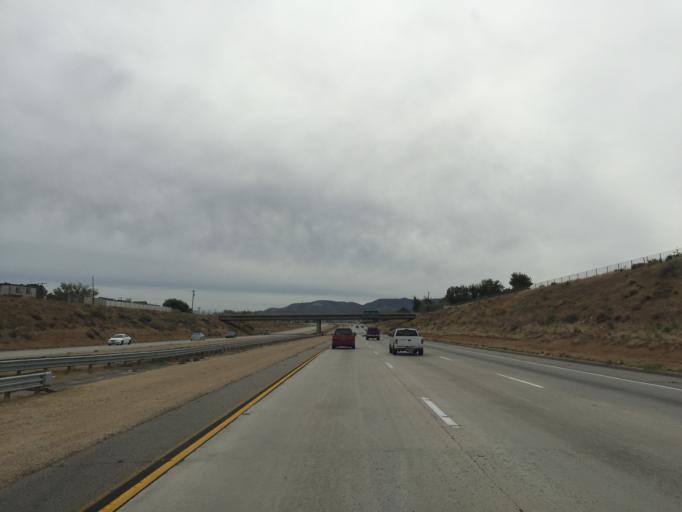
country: US
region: California
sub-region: Los Angeles County
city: Desert View Highlands
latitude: 34.6186
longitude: -118.1534
